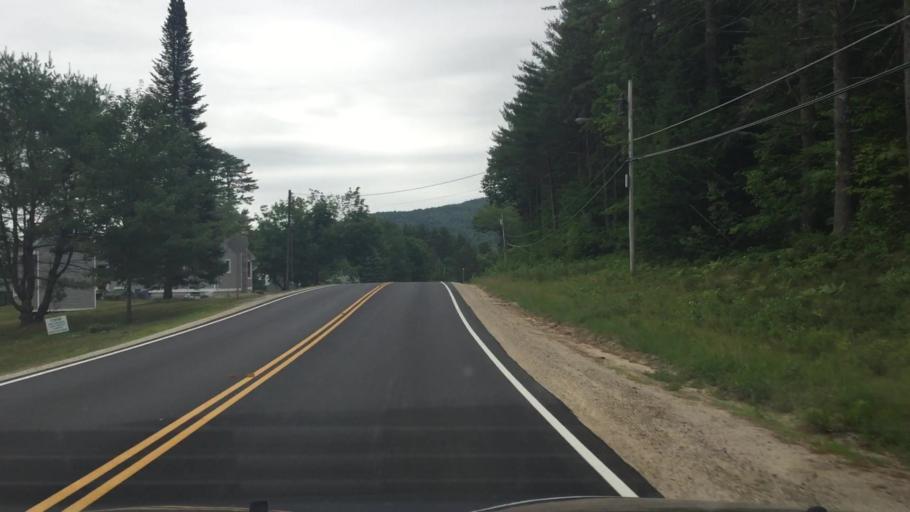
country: US
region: New Hampshire
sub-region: Carroll County
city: Freedom
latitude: 43.8049
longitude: -71.0609
